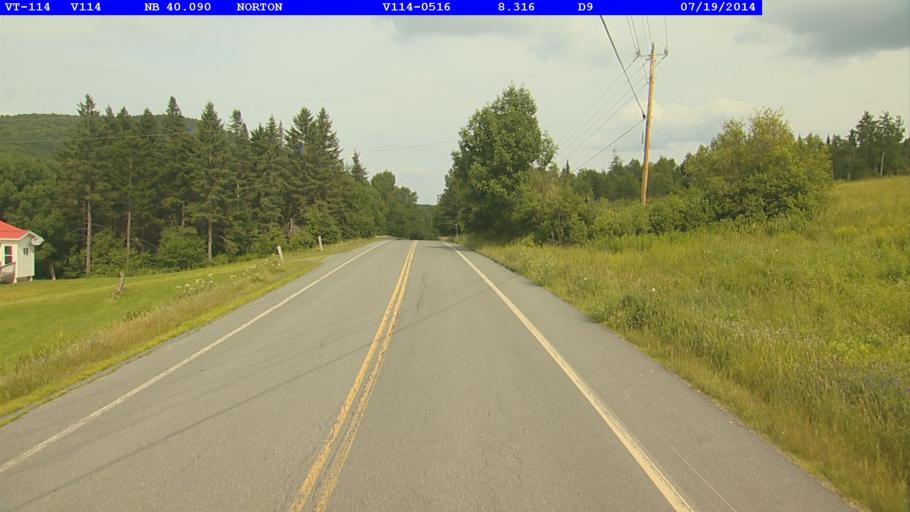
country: CA
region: Quebec
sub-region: Estrie
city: Coaticook
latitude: 44.9960
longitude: -71.7395
